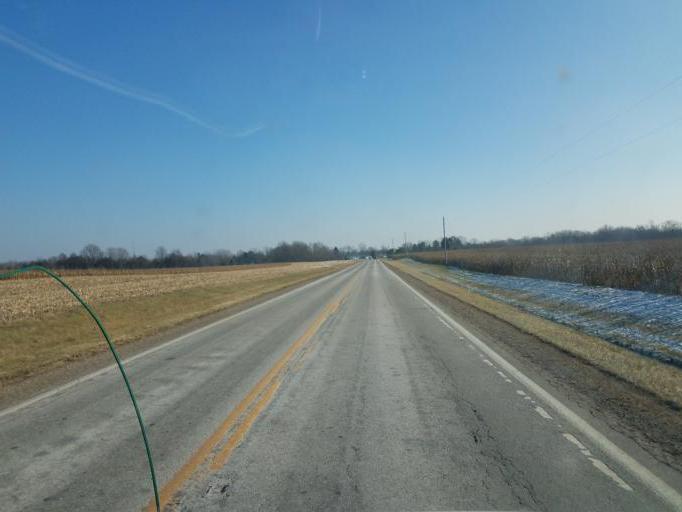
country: US
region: Ohio
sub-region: Morrow County
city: Cardington
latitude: 40.5089
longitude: -82.9117
